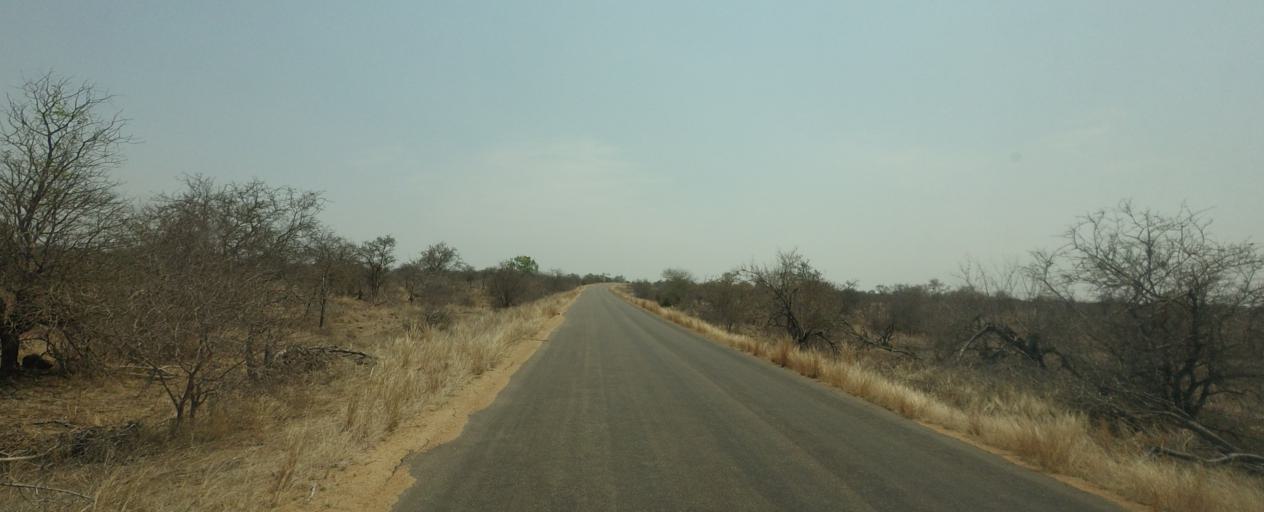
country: ZA
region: Limpopo
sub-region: Mopani District Municipality
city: Phalaborwa
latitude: -24.1199
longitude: 31.6989
